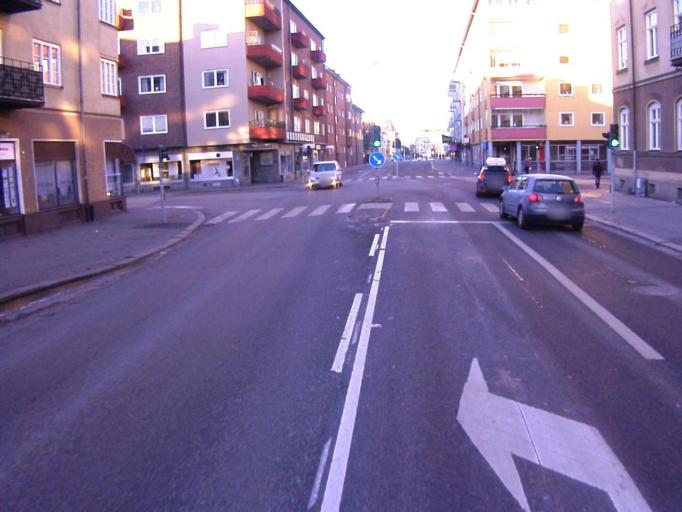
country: SE
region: Soedermanland
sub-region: Eskilstuna Kommun
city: Eskilstuna
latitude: 59.3677
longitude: 16.5227
